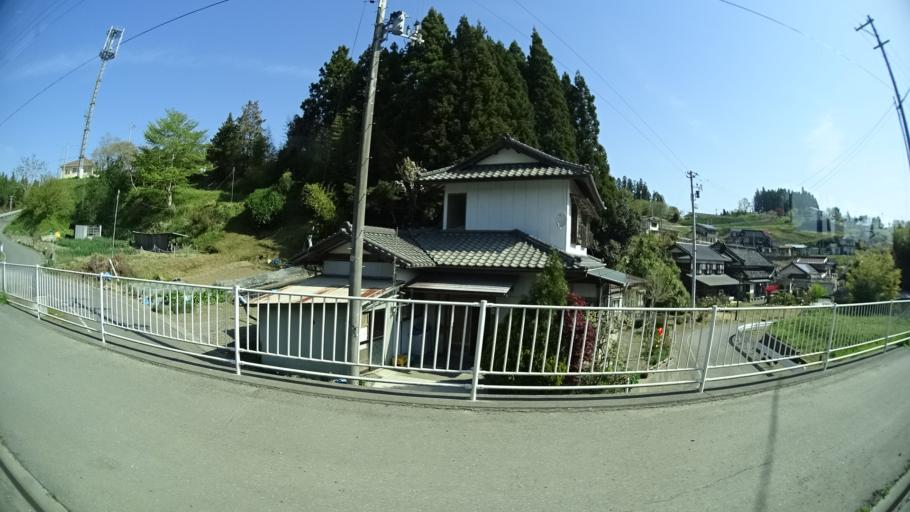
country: JP
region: Iwate
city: Ofunato
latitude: 38.9864
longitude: 141.6171
